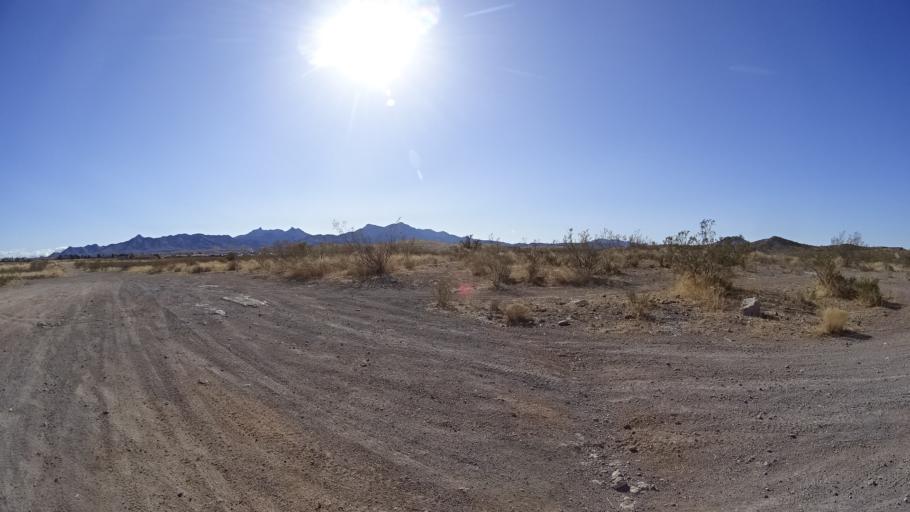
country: US
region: Arizona
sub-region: Mohave County
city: Kingman
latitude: 35.1885
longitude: -114.0234
